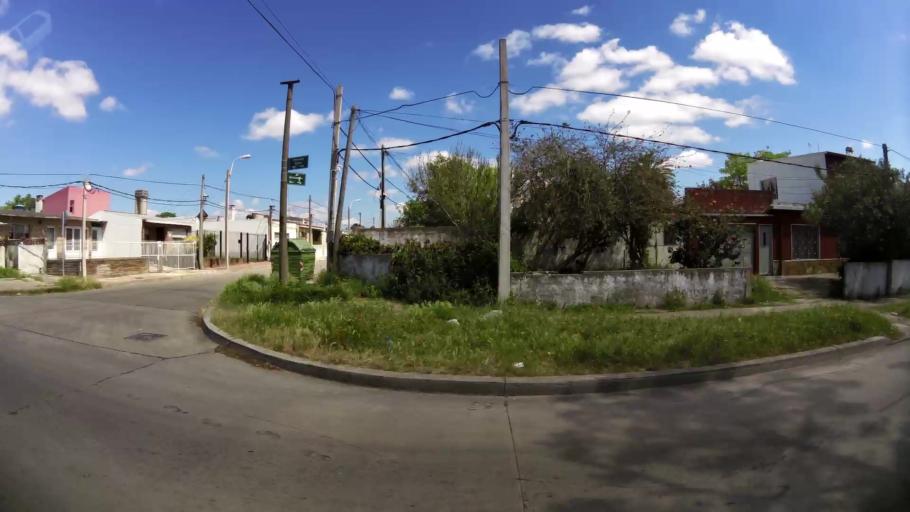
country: UY
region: Montevideo
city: Montevideo
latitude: -34.8521
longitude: -56.1372
